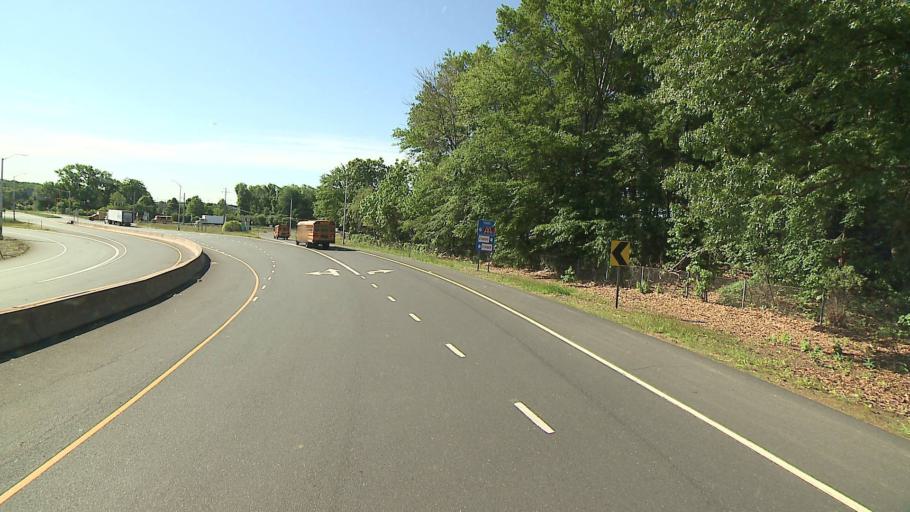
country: US
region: Connecticut
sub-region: Hartford County
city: South Windsor
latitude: 41.8046
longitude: -72.6172
